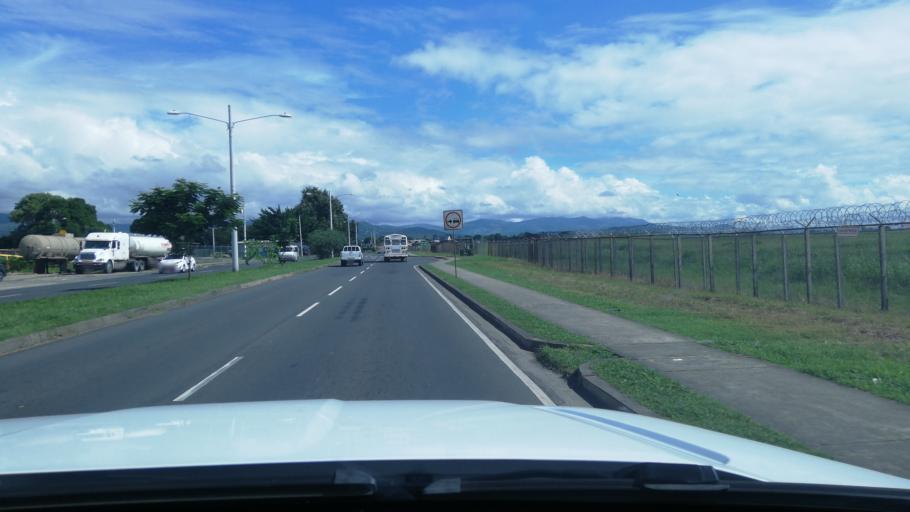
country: PA
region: Panama
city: Tocumen
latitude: 9.0812
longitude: -79.3849
